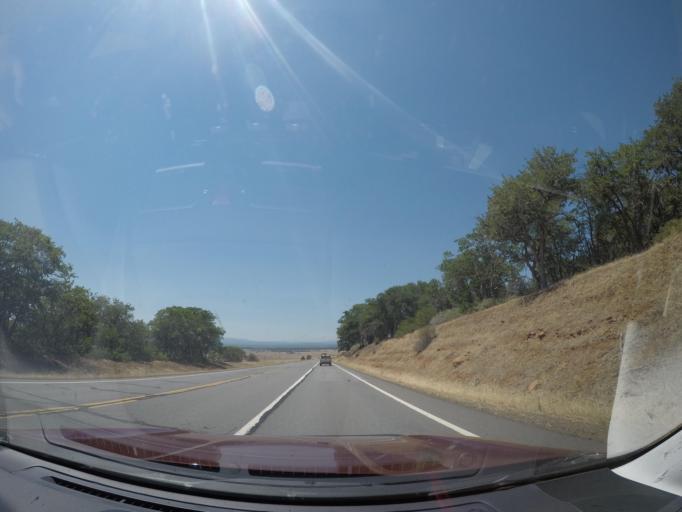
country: US
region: California
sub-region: Shasta County
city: Burney
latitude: 41.0937
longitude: -121.2765
